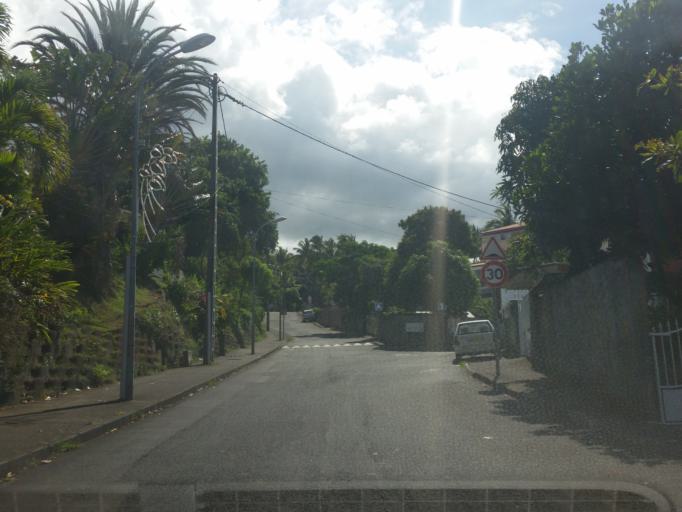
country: RE
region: Reunion
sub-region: Reunion
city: Sainte-Marie
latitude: -20.9150
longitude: 55.5076
